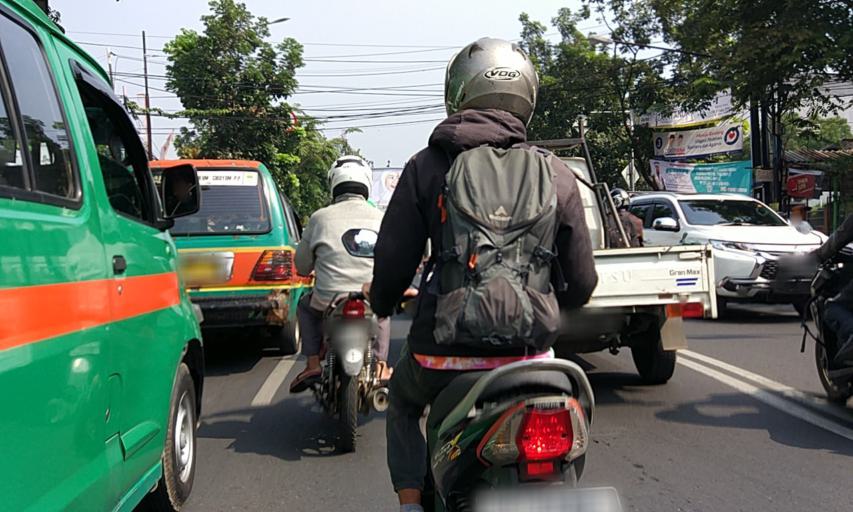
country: ID
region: West Java
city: Bandung
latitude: -6.8986
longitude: 107.6375
